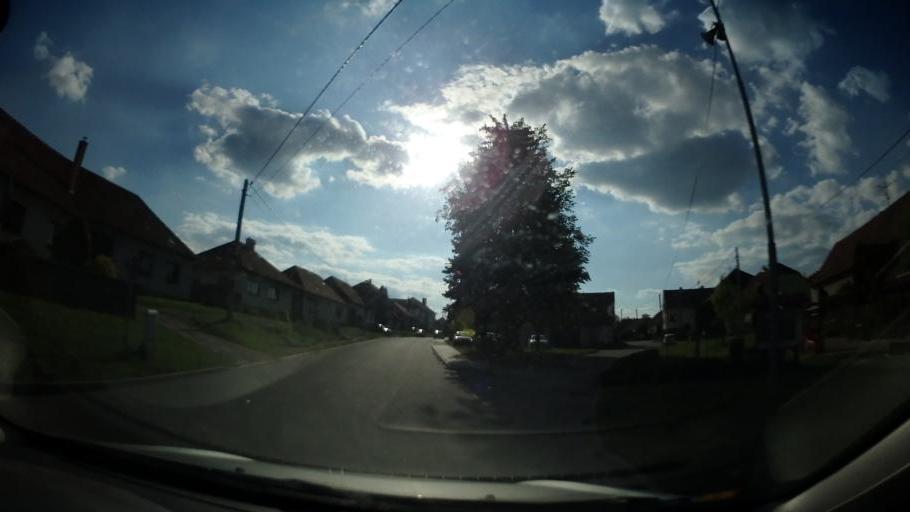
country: CZ
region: Vysocina
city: Budisov
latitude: 49.2938
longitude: 15.9883
